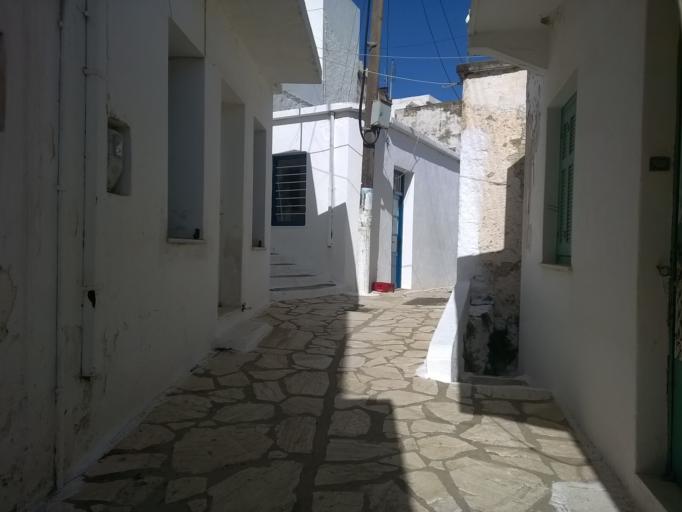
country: GR
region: South Aegean
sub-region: Nomos Kykladon
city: Filotion
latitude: 37.1455
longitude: 25.5294
